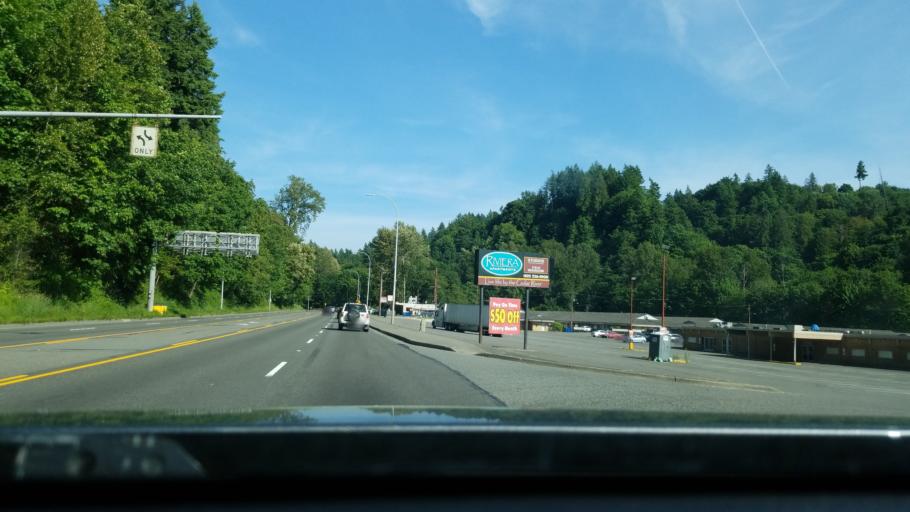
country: US
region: Washington
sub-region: King County
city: Renton
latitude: 47.4785
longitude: -122.1889
